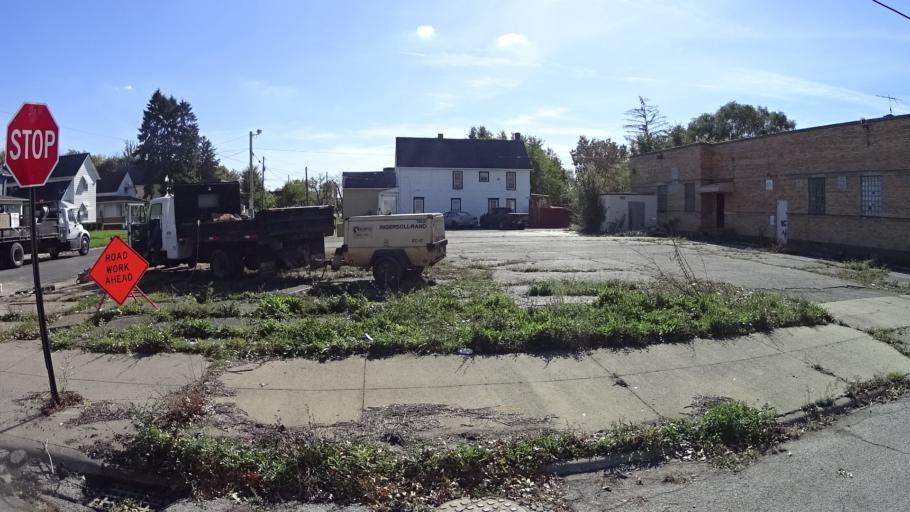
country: US
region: Ohio
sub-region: Lorain County
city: Lorain
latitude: 41.4551
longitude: -82.1737
